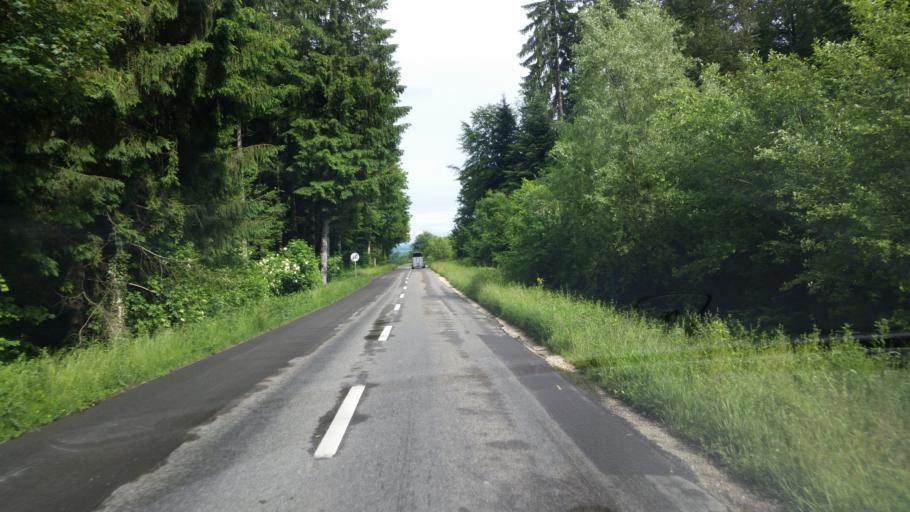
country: CH
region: Aargau
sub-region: Bezirk Muri
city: Waltenschwil
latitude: 47.3385
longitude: 8.3243
